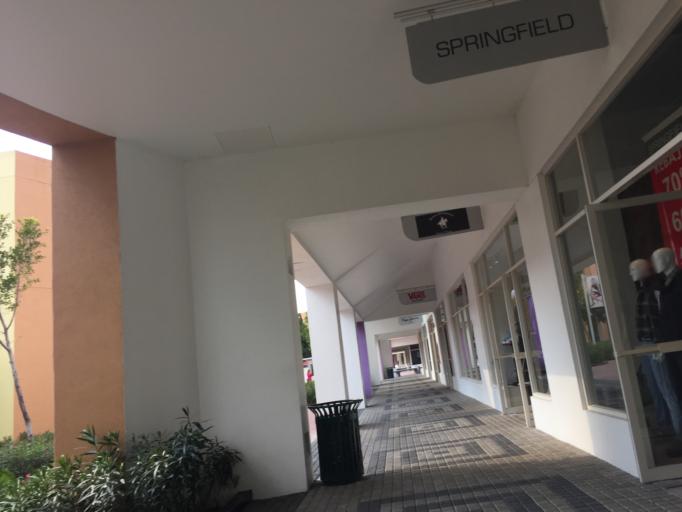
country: MX
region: Mexico
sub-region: Tultitlan
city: Buenavista
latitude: 19.6005
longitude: -99.1986
